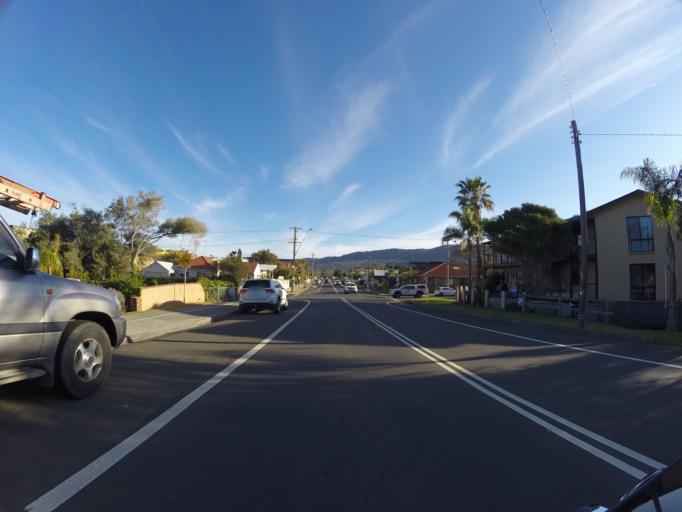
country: AU
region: New South Wales
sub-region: Wollongong
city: Bulli
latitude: -34.3122
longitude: 150.9291
